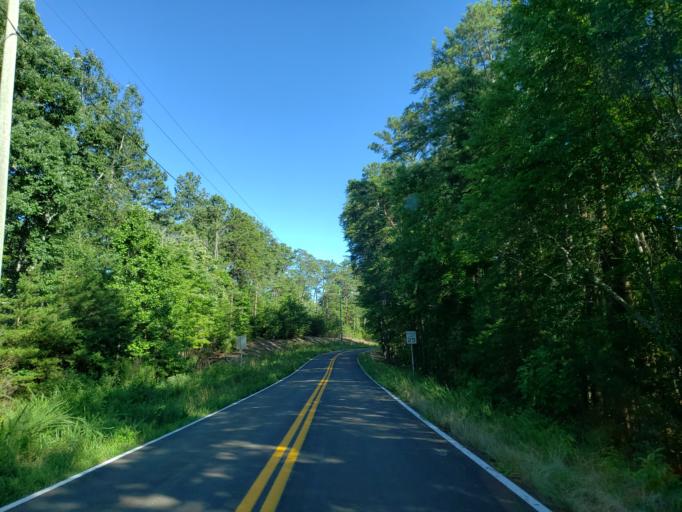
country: US
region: Georgia
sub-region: Bartow County
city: Rydal
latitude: 34.3680
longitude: -84.6198
